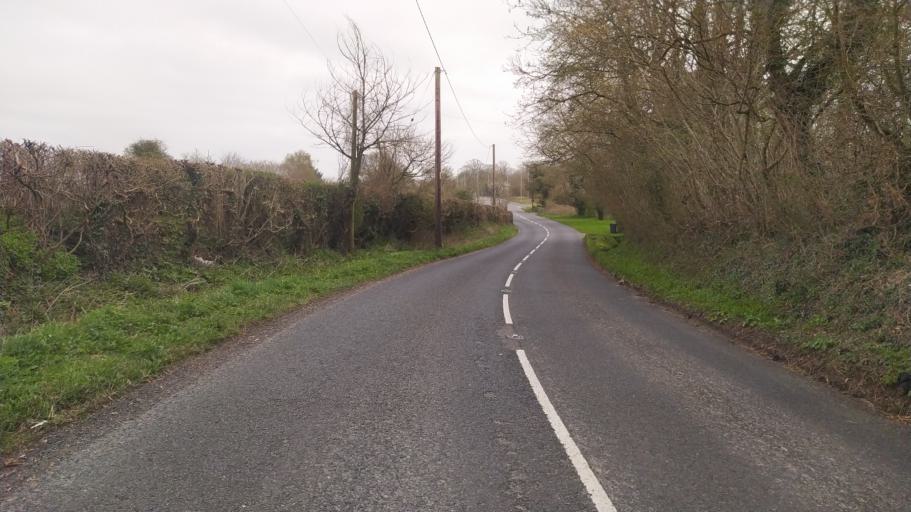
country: GB
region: England
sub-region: Wiltshire
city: Southwick
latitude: 51.3155
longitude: -2.2325
